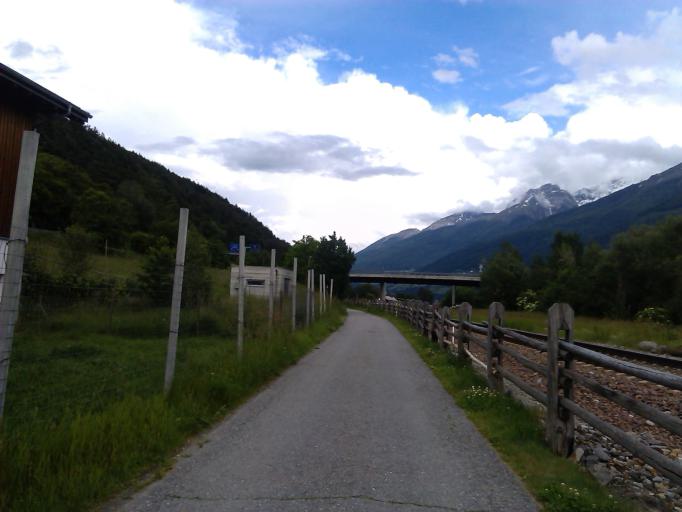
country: IT
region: Trentino-Alto Adige
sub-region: Bolzano
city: Prato Allo Stelvio
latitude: 46.6364
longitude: 10.6050
